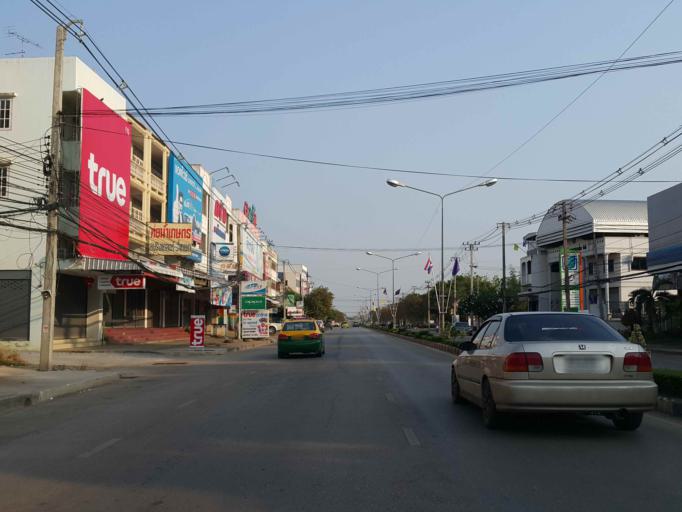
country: TH
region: Sukhothai
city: Sawankhalok
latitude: 17.3086
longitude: 99.8316
